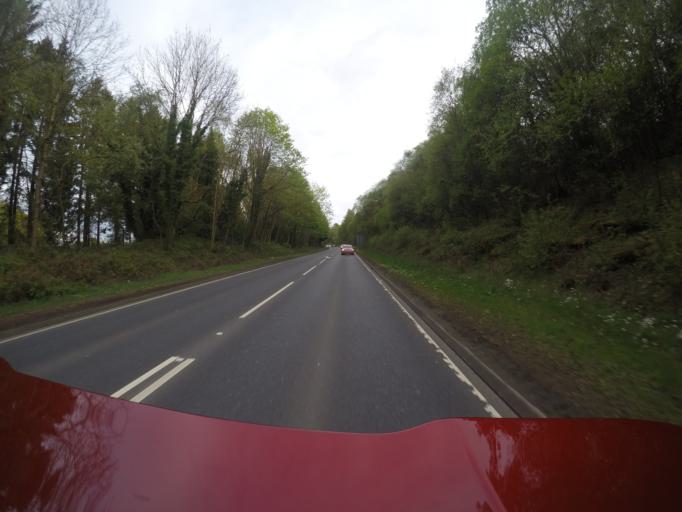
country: GB
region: Scotland
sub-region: West Dunbartonshire
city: Balloch
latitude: 56.0112
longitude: -4.6097
